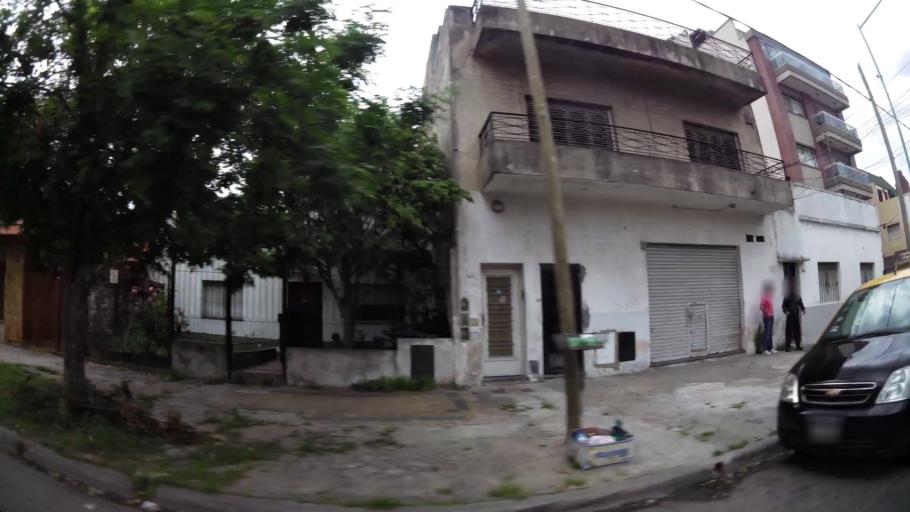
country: AR
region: Buenos Aires
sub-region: Partido de Lanus
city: Lanus
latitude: -34.6903
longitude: -58.3946
